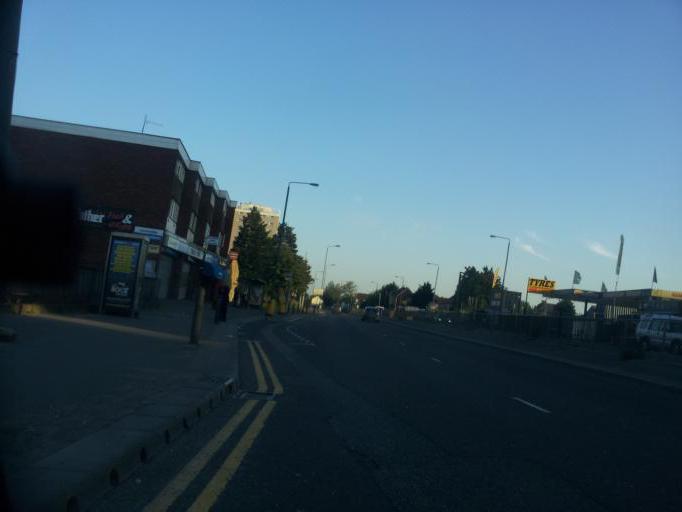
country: GB
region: England
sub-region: Greater London
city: Erith
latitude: 51.4724
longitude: 0.1812
